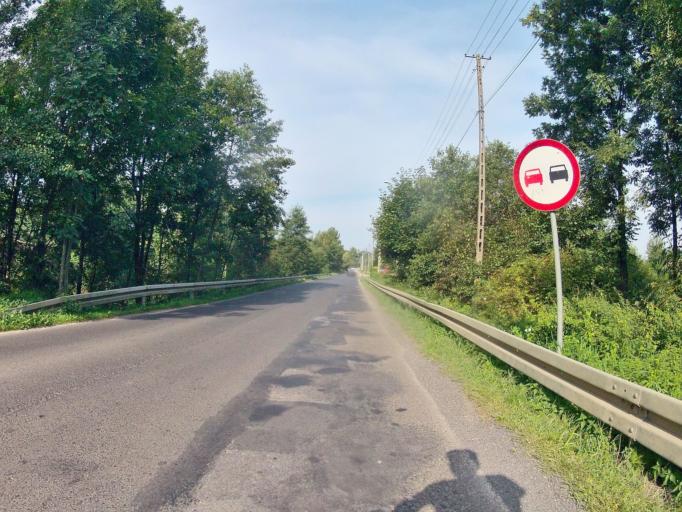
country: PL
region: Subcarpathian Voivodeship
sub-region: Powiat jasielski
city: Trzcinica
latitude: 49.7621
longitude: 21.4317
